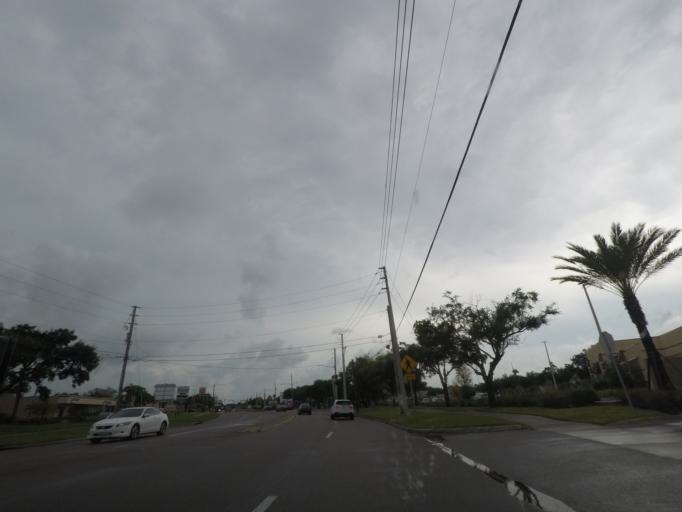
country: US
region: Florida
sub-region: Pinellas County
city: Kenneth City
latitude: 27.7917
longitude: -82.7311
